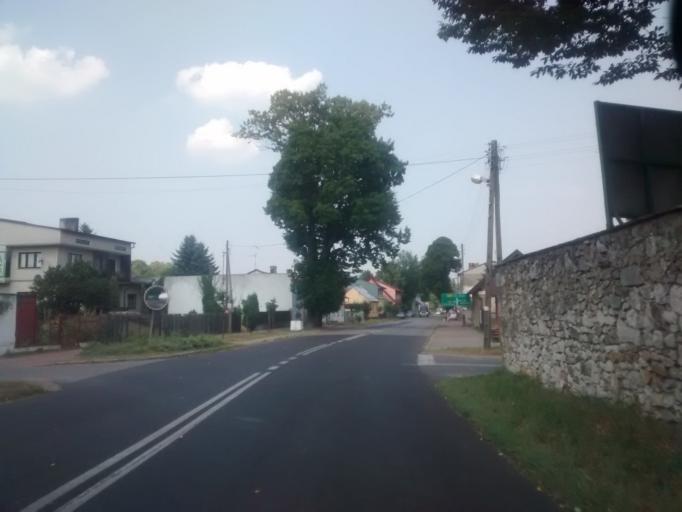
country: PL
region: Silesian Voivodeship
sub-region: Powiat czestochowski
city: Potok Zloty
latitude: 50.7188
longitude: 19.4359
